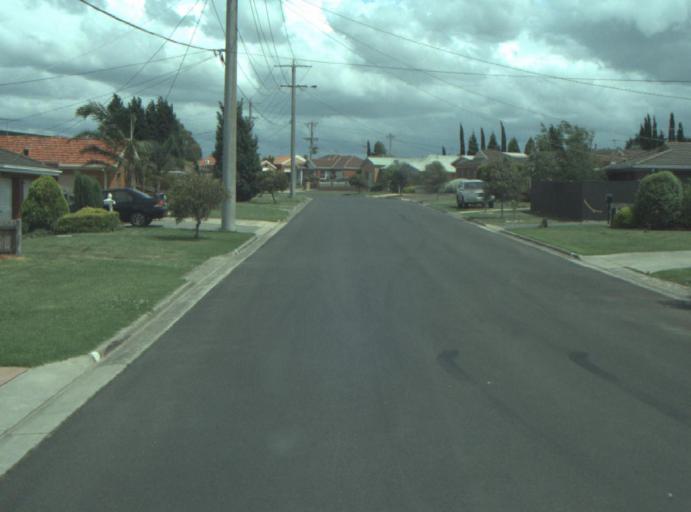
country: AU
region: Victoria
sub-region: Greater Geelong
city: Bell Park
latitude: -38.0937
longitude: 144.3414
